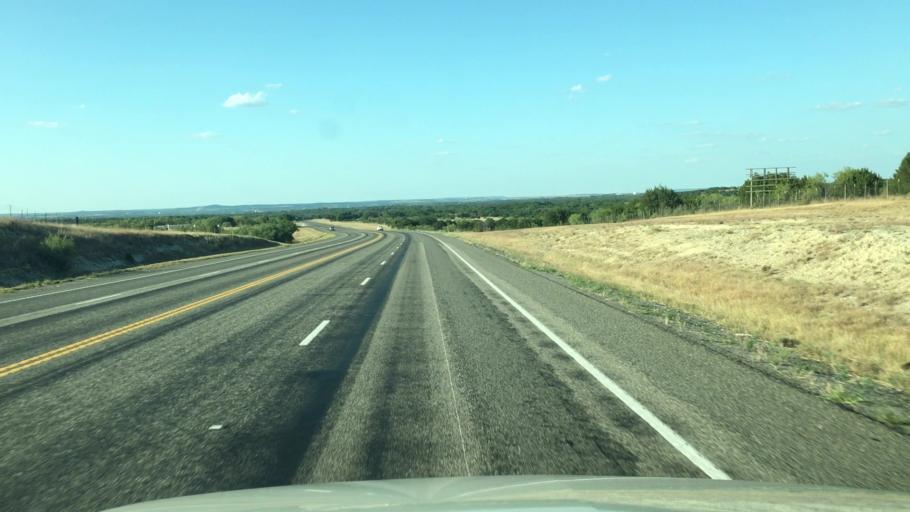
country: US
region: Texas
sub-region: Lampasas County
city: Lampasas
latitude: 30.9970
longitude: -98.1962
